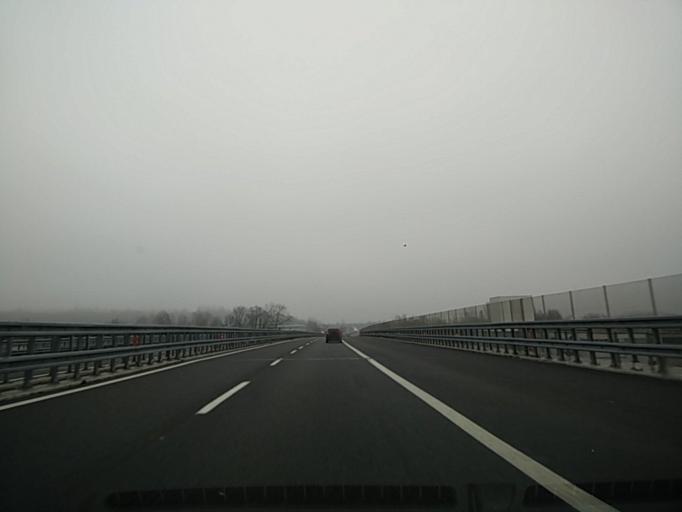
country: IT
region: Piedmont
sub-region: Provincia di Asti
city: Asti
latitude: 44.9135
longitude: 8.2289
